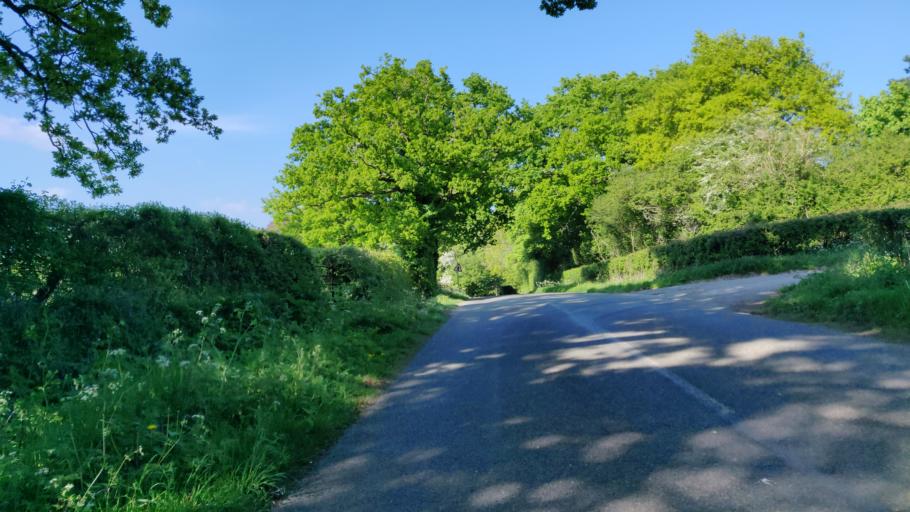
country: GB
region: England
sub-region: West Sussex
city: Southwater
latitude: 51.0445
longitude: -0.3540
